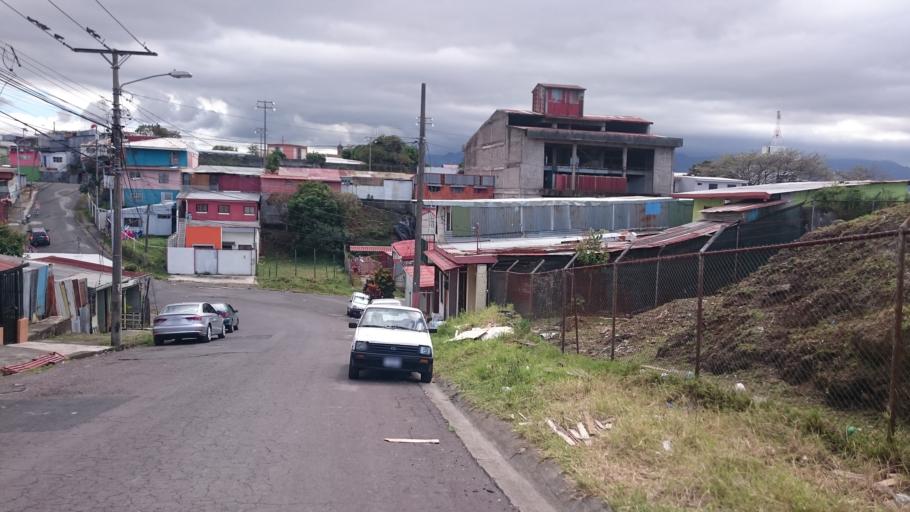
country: CR
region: San Jose
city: Calle Blancos
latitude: 9.9441
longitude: -84.0716
